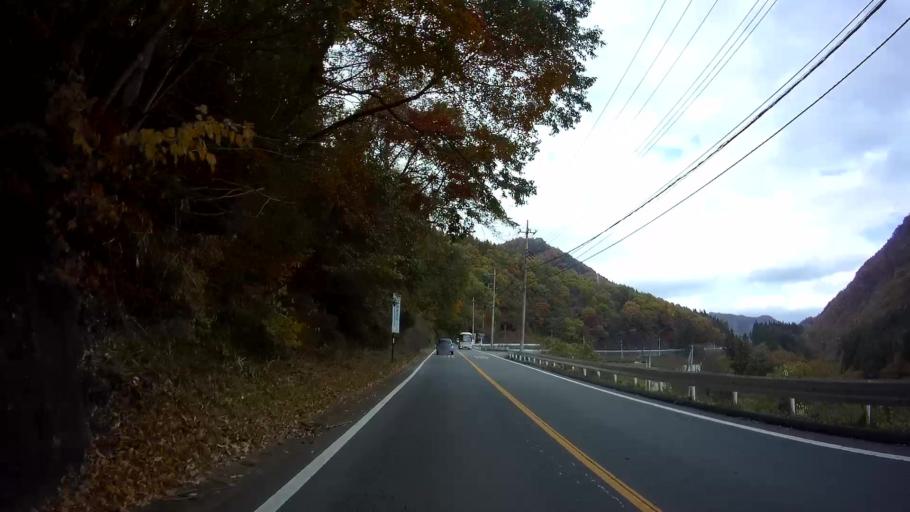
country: JP
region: Gunma
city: Nakanojomachi
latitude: 36.5831
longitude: 138.6232
